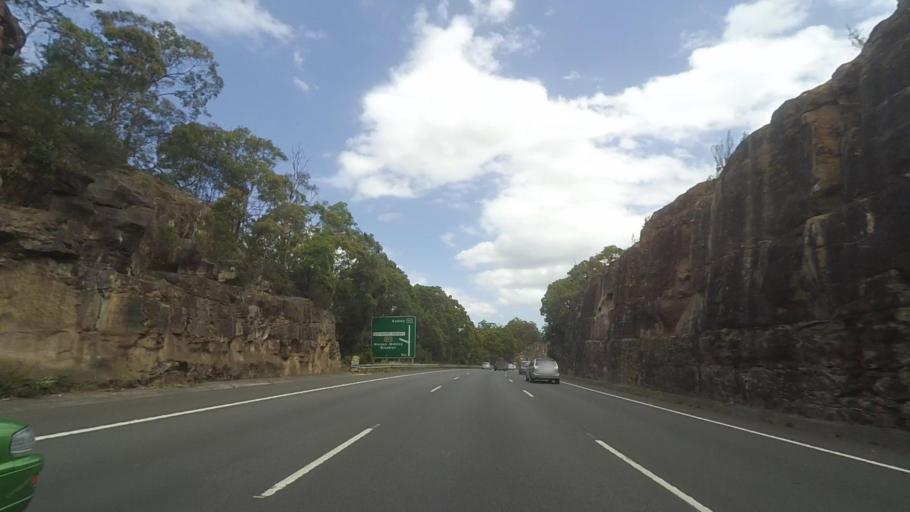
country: AU
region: New South Wales
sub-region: Hornsby Shire
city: Berowra Heights
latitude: -33.5173
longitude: 151.1962
